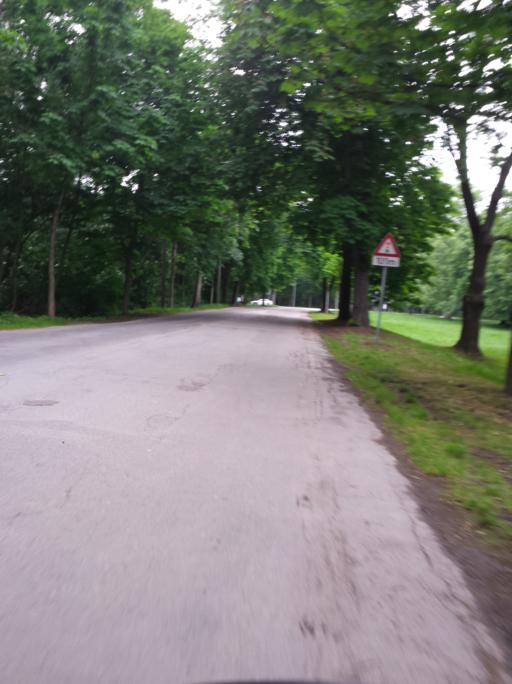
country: AT
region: Vienna
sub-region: Wien Stadt
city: Vienna
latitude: 48.2010
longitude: 16.4172
